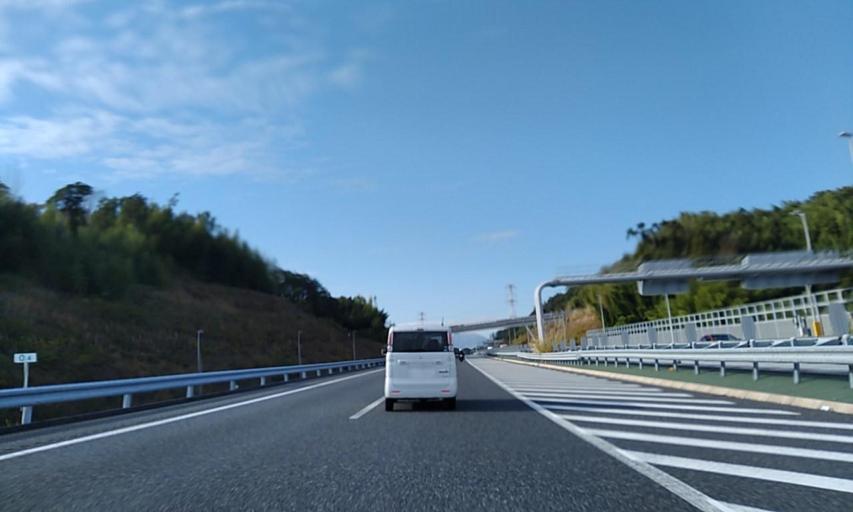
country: JP
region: Mie
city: Yokkaichi
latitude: 35.0400
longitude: 136.6245
